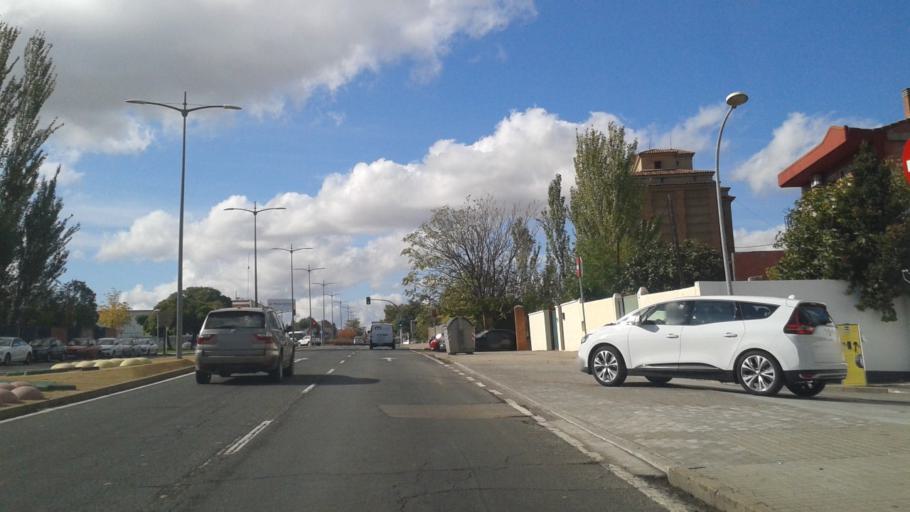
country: ES
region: Castille and Leon
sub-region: Provincia de Valladolid
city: Valladolid
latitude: 41.6610
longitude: -4.7460
